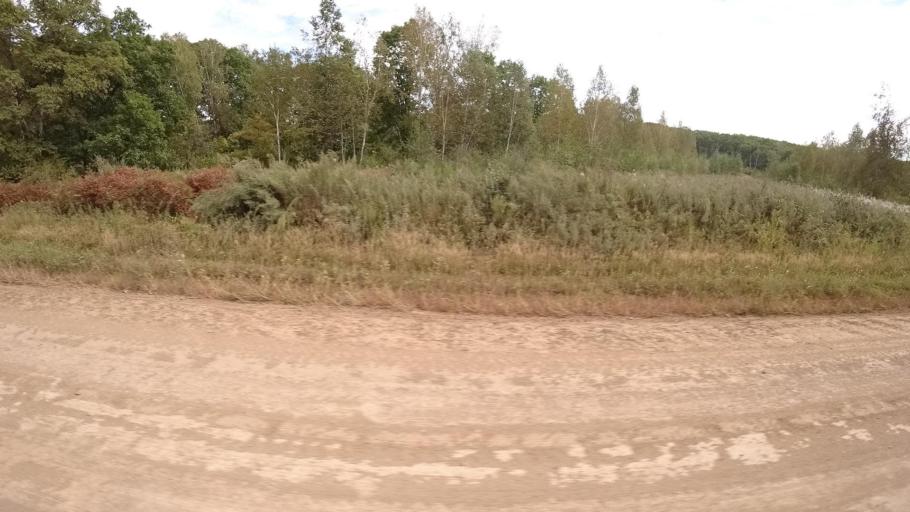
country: RU
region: Primorskiy
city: Yakovlevka
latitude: 44.4878
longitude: 133.5839
